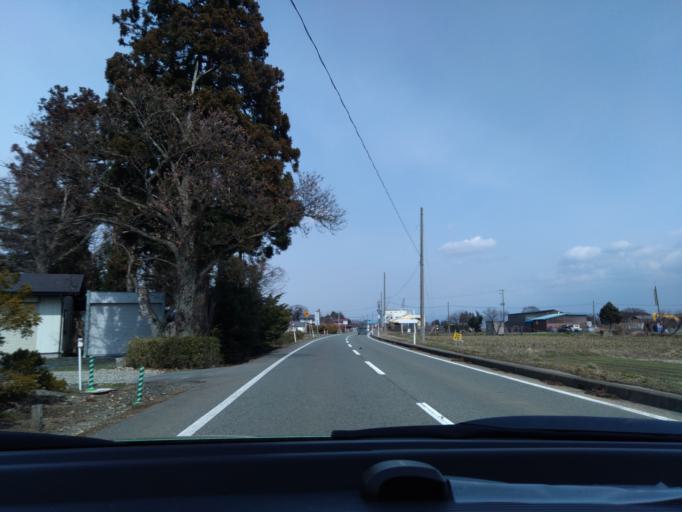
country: JP
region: Iwate
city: Morioka-shi
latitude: 39.6108
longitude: 141.1130
